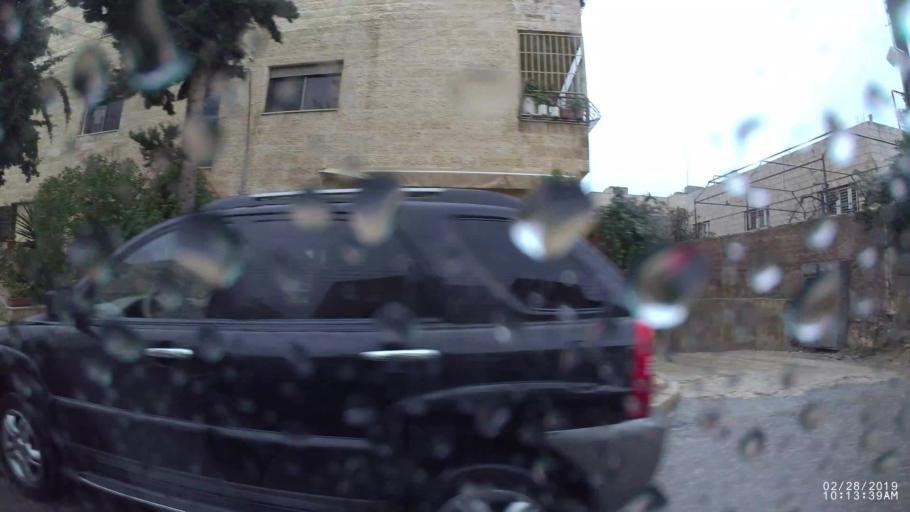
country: JO
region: Amman
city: Al Jubayhah
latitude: 32.0124
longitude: 35.8879
